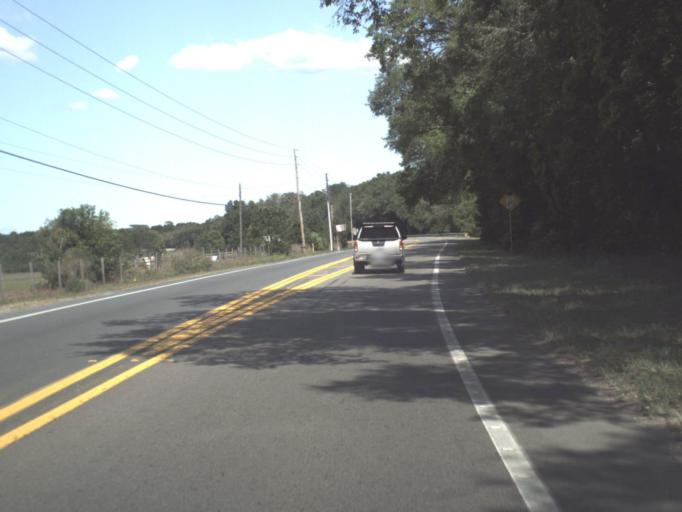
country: US
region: Florida
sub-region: Lake County
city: Mount Plymouth
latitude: 28.8042
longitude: -81.5763
